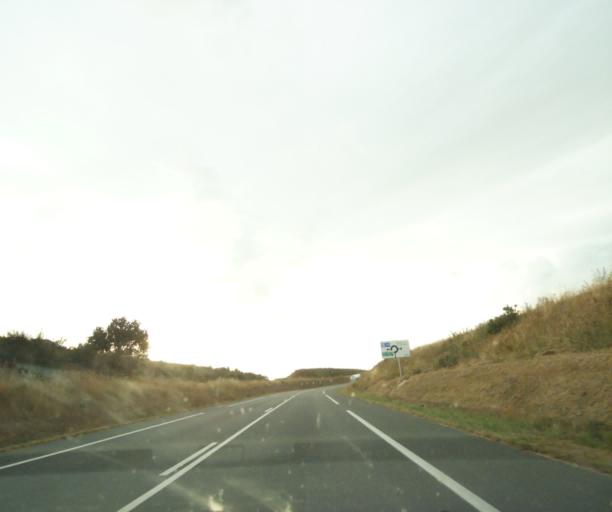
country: FR
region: Pays de la Loire
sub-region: Departement de la Vendee
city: Saint-Hilaire-de-Talmont
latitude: 46.4727
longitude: -1.6509
